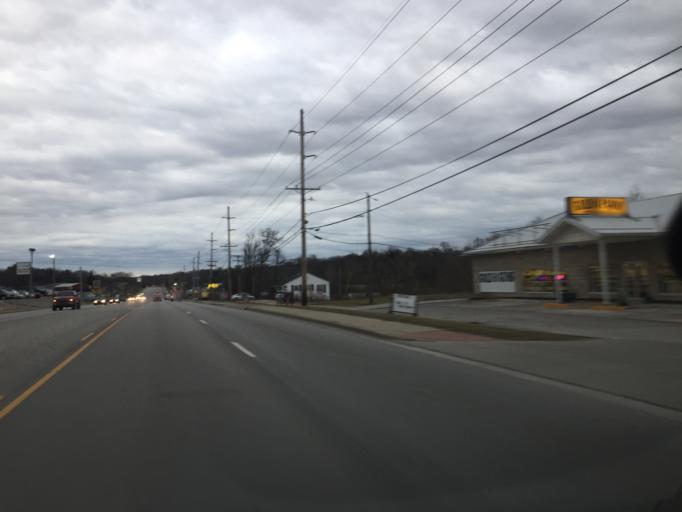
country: US
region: Indiana
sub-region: Monroe County
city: Ellettsville
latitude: 39.2227
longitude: -86.6084
